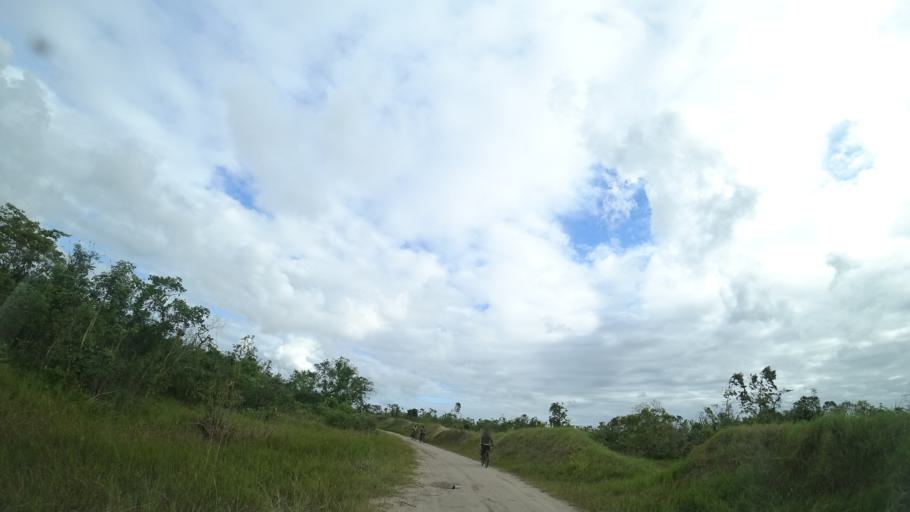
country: MZ
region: Sofala
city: Beira
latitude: -19.6168
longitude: 35.0608
